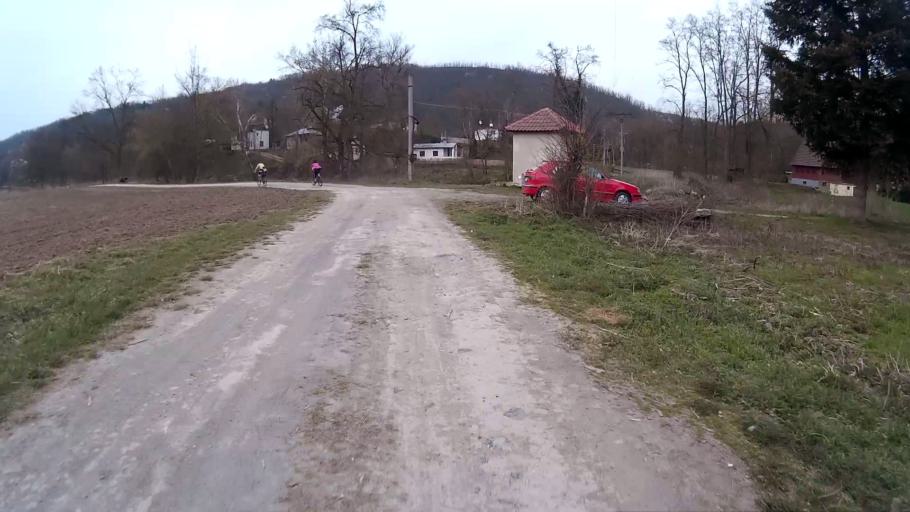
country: CZ
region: South Moravian
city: Ivancice
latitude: 49.0958
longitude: 16.3949
